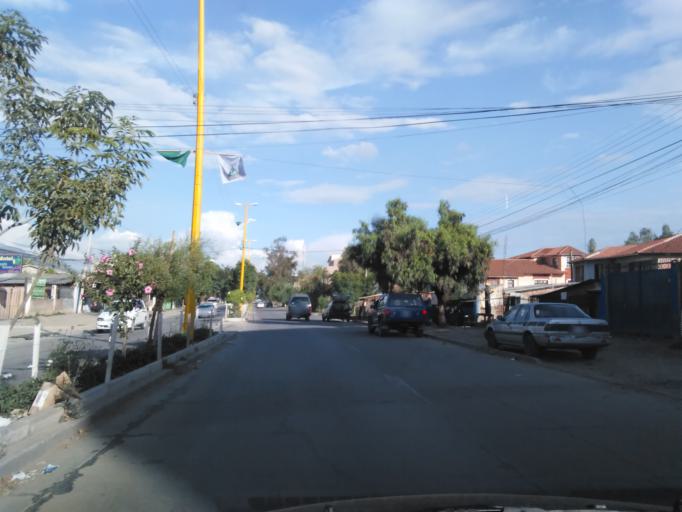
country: BO
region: Cochabamba
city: Cochabamba
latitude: -17.3460
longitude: -66.2029
